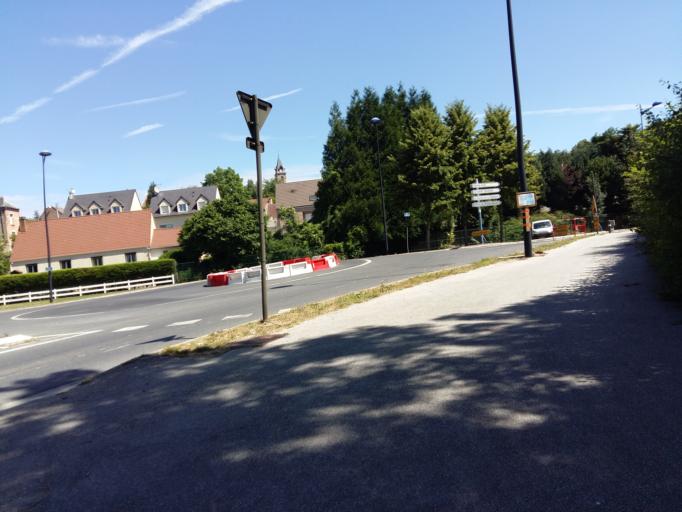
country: FR
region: Picardie
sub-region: Departement de la Somme
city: Dreuil-les-Amiens
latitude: 49.9214
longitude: 2.2607
